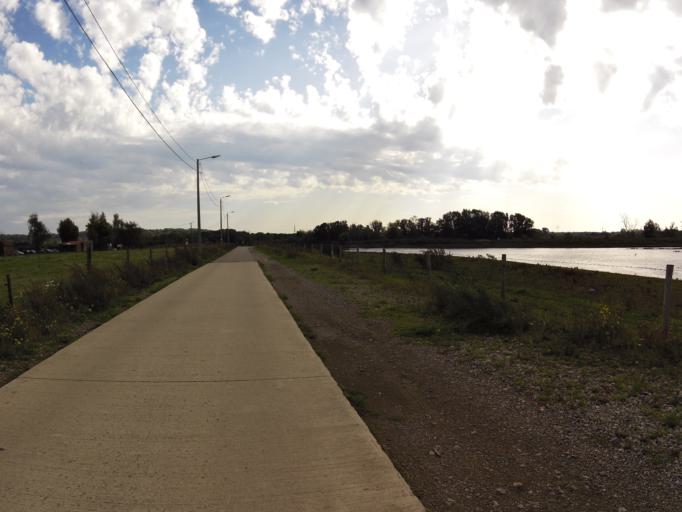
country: NL
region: Limburg
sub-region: Gemeente Meerssen
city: Meerssen
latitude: 50.9106
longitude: 5.7126
